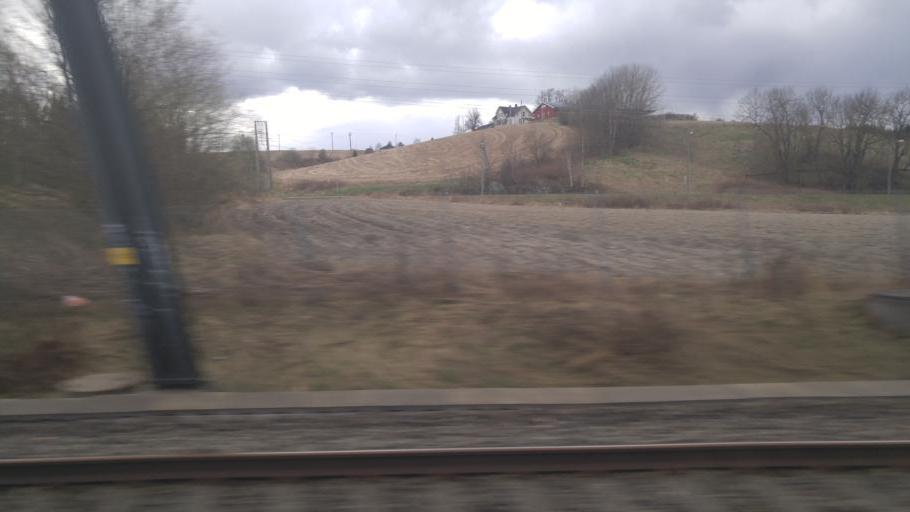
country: NO
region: Akershus
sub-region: Skedsmo
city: Lillestrom
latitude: 59.9722
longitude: 11.0690
